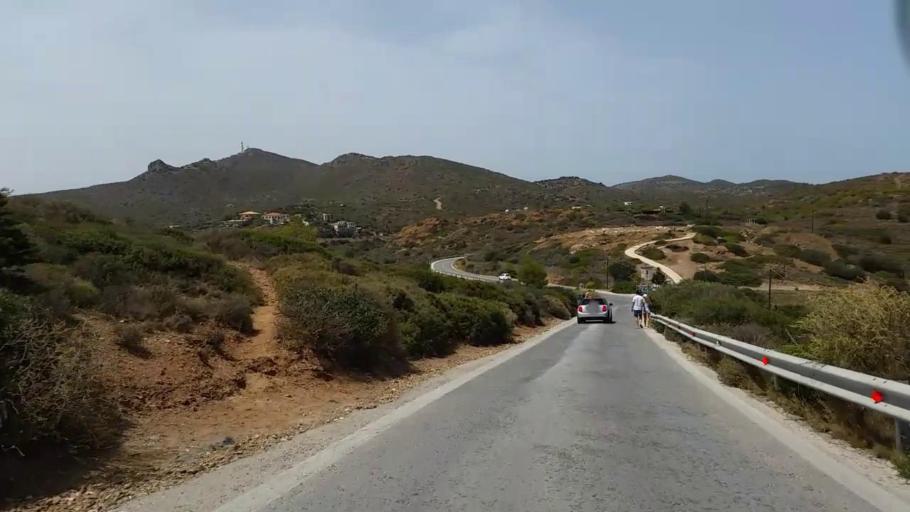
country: GR
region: Attica
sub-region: Nomarchia Anatolikis Attikis
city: Lavrio
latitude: 37.6510
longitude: 24.0264
